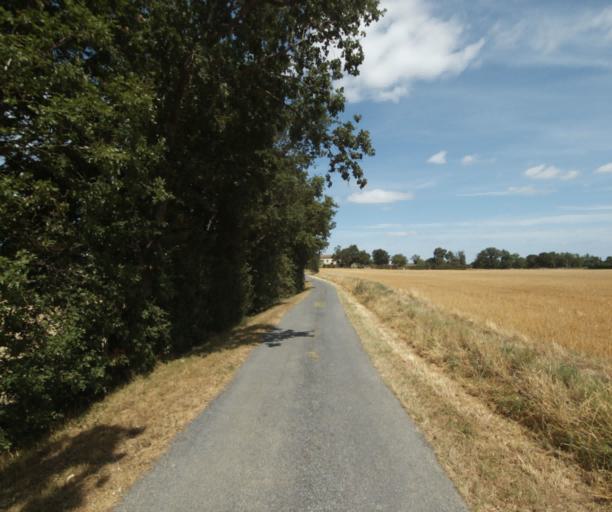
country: FR
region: Midi-Pyrenees
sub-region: Departement du Tarn
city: Dourgne
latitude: 43.4978
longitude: 2.0970
